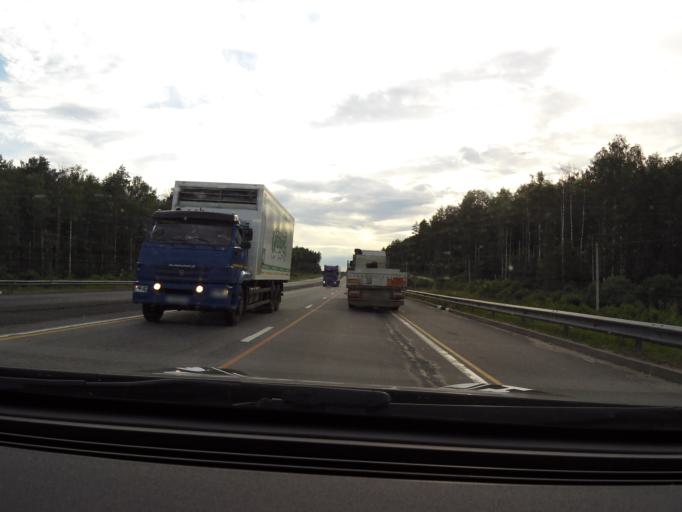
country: RU
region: Vladimir
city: Orgtrud
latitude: 56.1035
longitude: 40.6793
